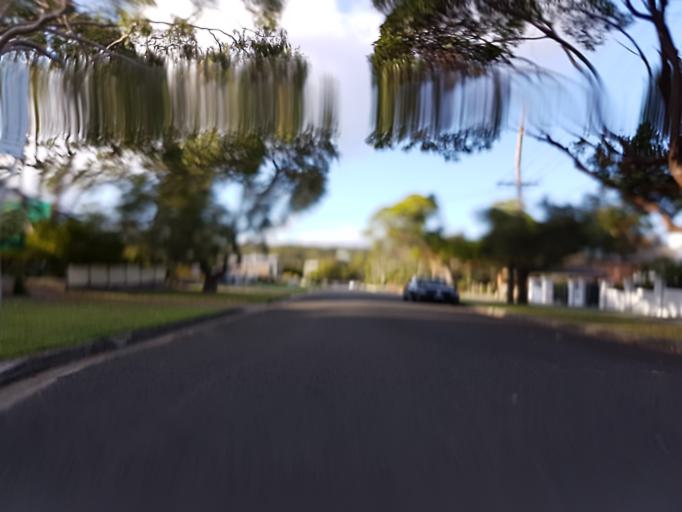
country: AU
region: New South Wales
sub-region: Manly Vale
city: Balgowlah
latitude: -33.7897
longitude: 151.2430
